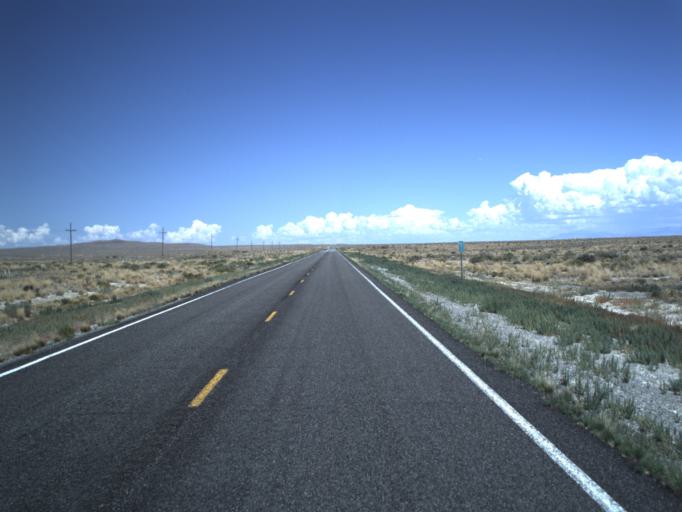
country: US
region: Utah
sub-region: Millard County
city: Delta
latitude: 39.1099
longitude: -113.1382
